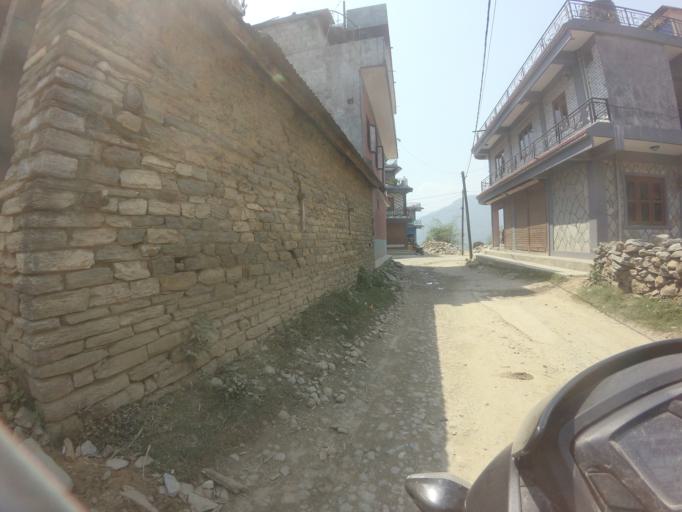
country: NP
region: Western Region
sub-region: Gandaki Zone
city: Pokhara
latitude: 28.3094
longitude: 83.9589
